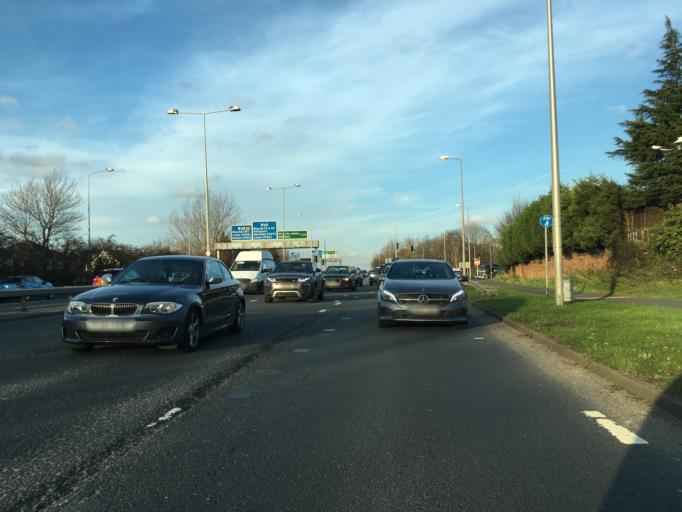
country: GB
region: England
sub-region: Manchester
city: Didsbury
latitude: 53.3943
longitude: -2.2265
